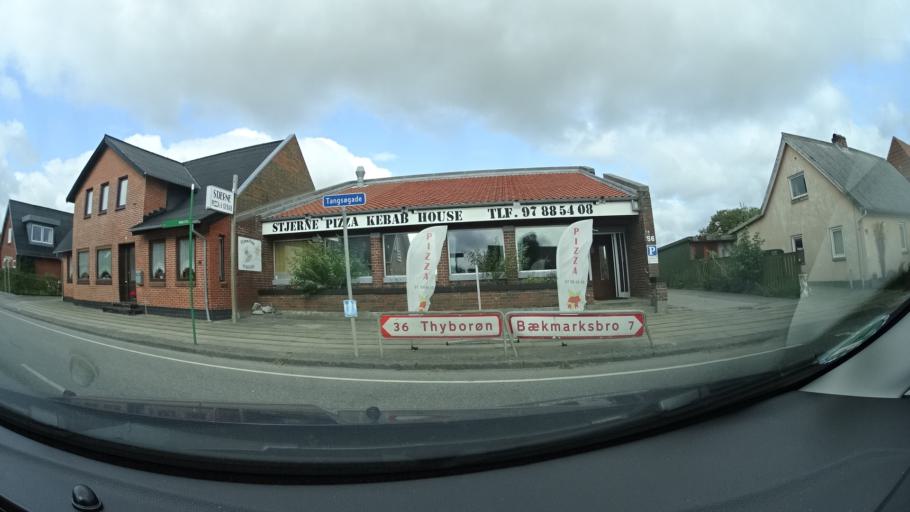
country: DK
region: Central Jutland
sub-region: Lemvig Kommune
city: Lemvig
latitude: 56.4365
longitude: 8.2023
